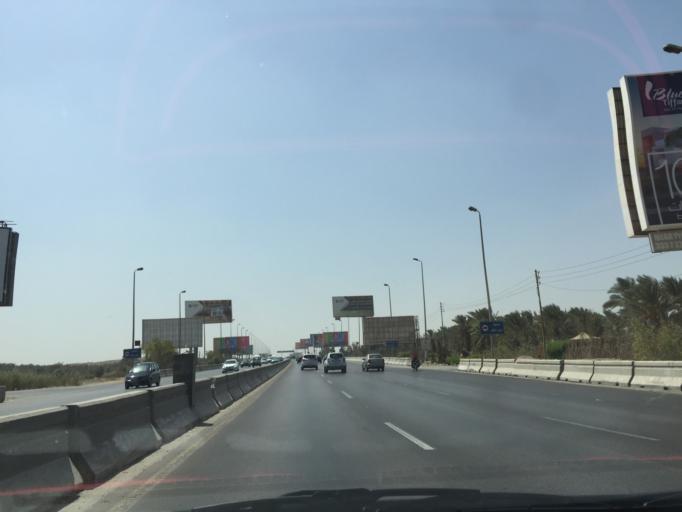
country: EG
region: Al Jizah
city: Awsim
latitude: 30.0550
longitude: 31.0725
